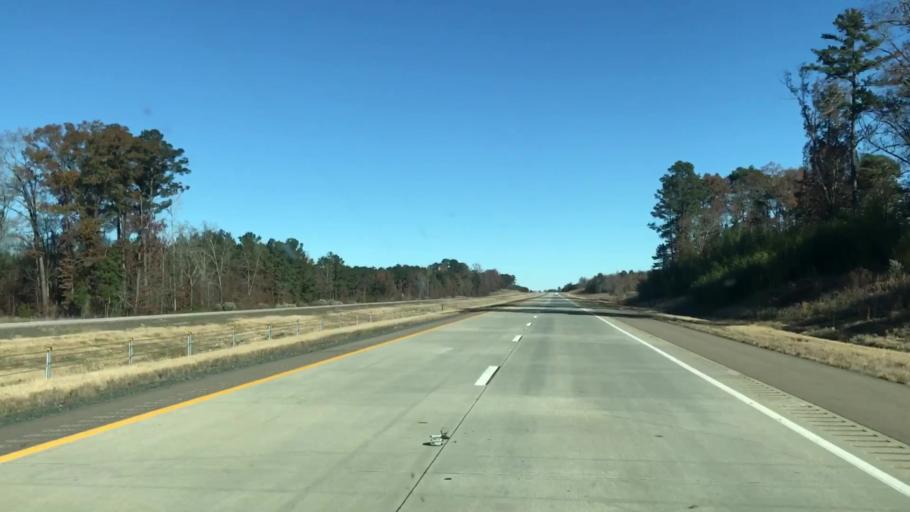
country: US
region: Louisiana
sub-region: Caddo Parish
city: Vivian
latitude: 33.0320
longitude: -93.9007
